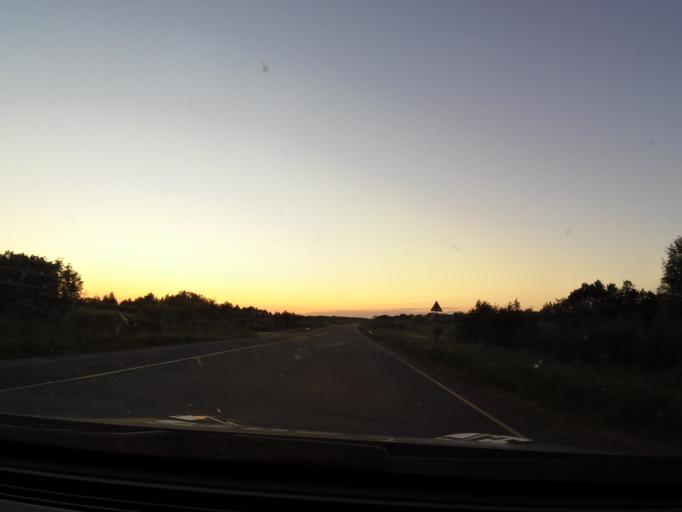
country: RU
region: Vologda
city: Vytegra
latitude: 60.9549
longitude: 36.0901
